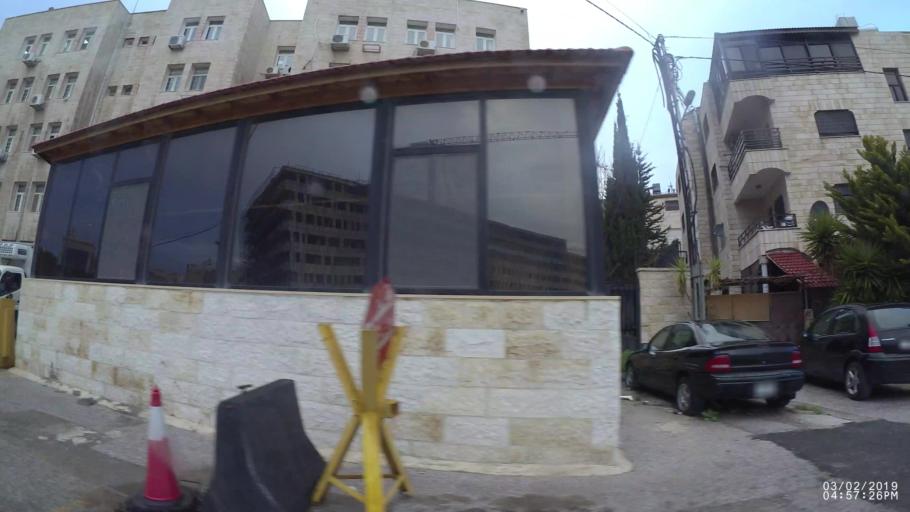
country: JO
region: Amman
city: Amman
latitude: 31.9784
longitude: 35.9072
